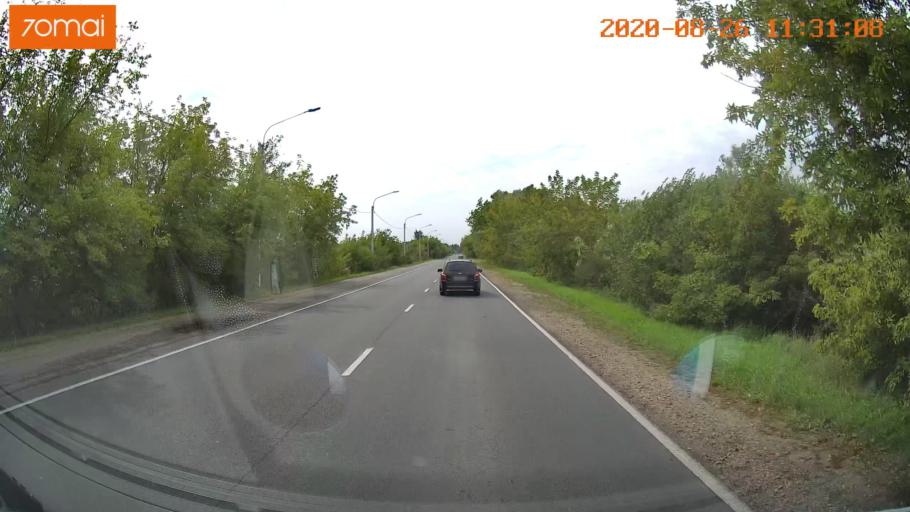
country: RU
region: Rjazan
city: Shilovo
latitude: 54.3093
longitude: 40.8762
